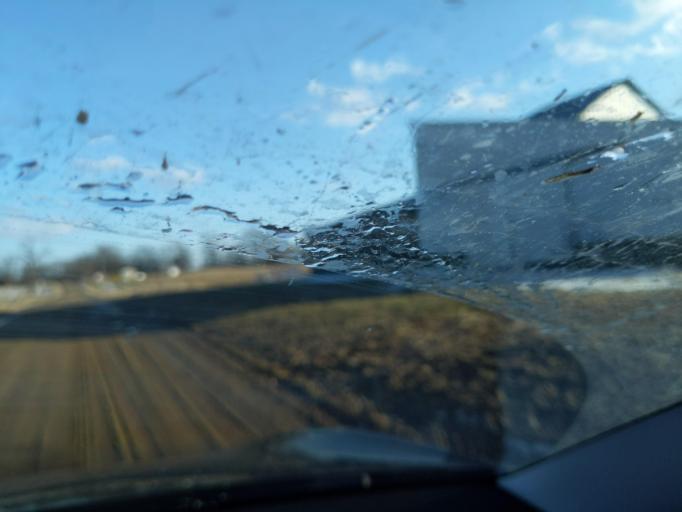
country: US
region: Michigan
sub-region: Ingham County
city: Stockbridge
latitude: 42.5205
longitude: -84.1853
